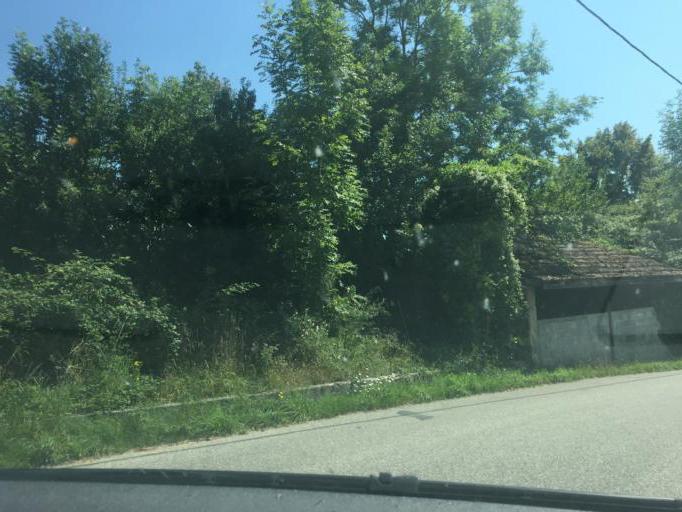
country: FR
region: Rhone-Alpes
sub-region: Departement de la Haute-Savoie
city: Sillingy
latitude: 45.9296
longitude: 5.9920
